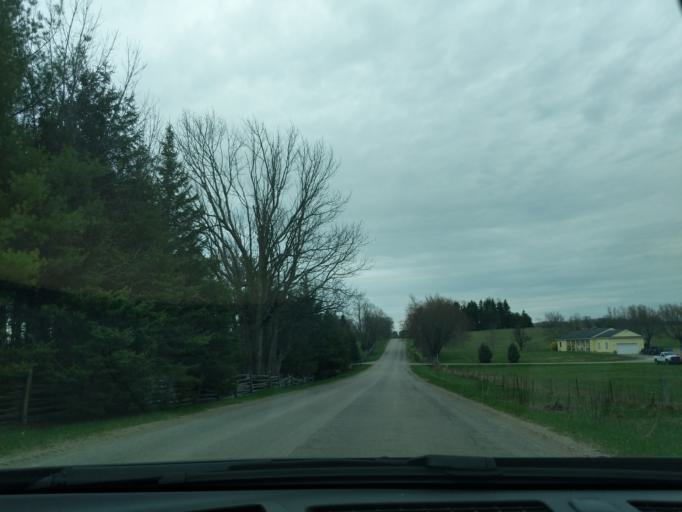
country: CA
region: Ontario
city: Orangeville
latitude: 44.0144
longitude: -79.9672
